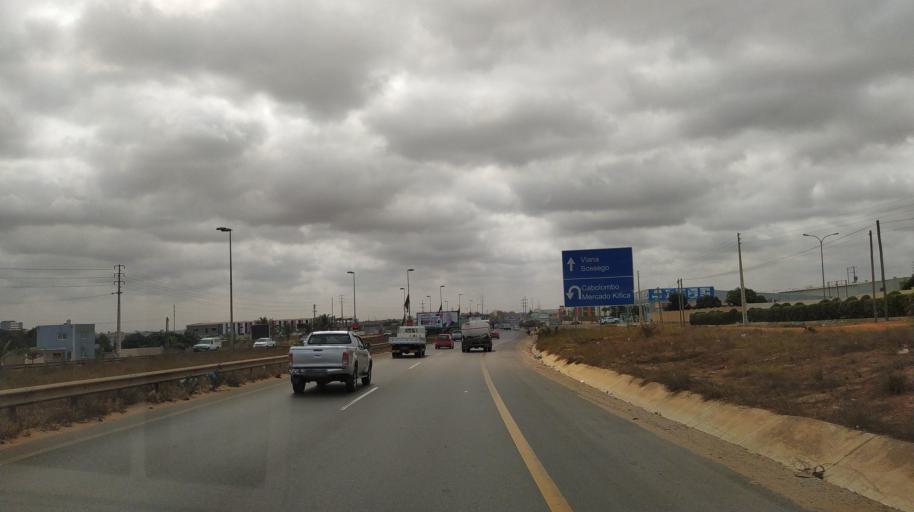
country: AO
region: Luanda
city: Luanda
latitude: -8.9766
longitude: 13.2005
